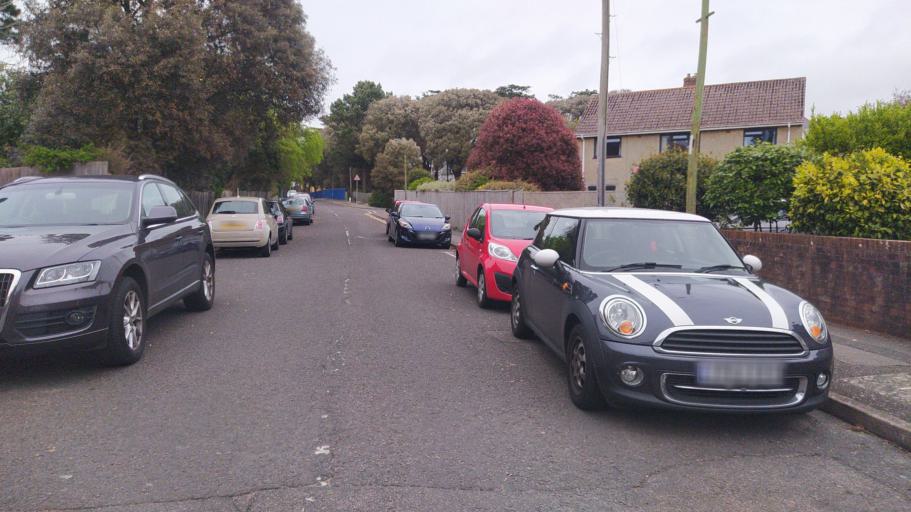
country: GB
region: England
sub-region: Dorset
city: Christchurch
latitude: 50.7218
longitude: -1.7923
